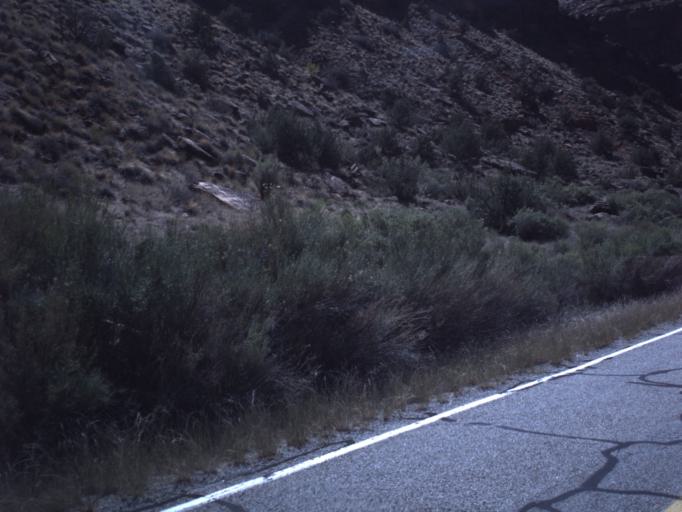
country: US
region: Utah
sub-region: Grand County
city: Moab
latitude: 38.7965
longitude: -109.3195
